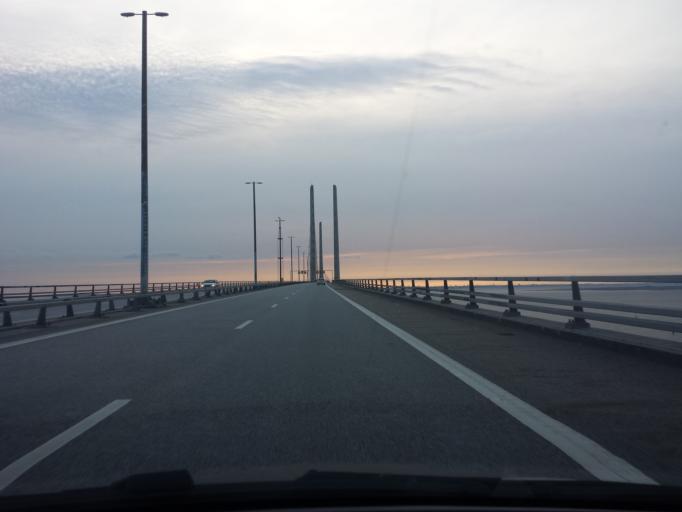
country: SE
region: Skane
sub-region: Malmo
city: Bunkeflostrand
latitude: 55.5718
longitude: 12.8433
